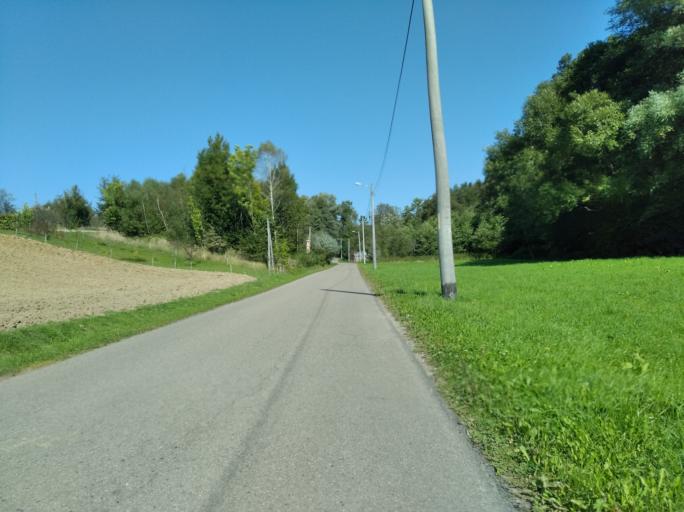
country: PL
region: Subcarpathian Voivodeship
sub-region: Powiat strzyzowski
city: Czudec
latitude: 49.9591
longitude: 21.8095
